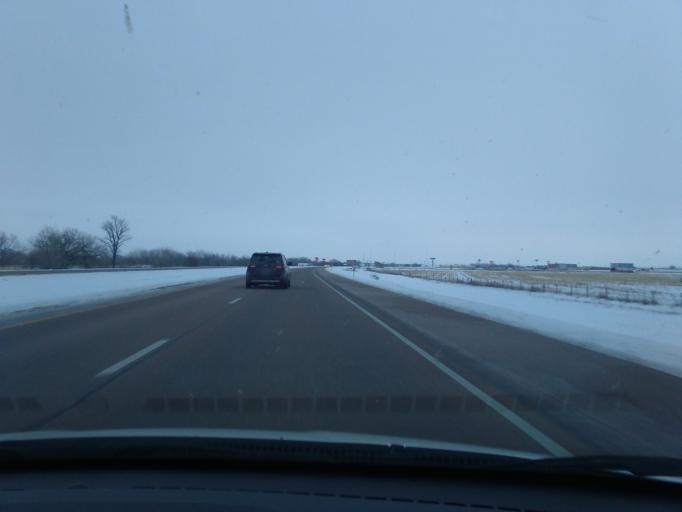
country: US
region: Nebraska
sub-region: Keith County
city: Ogallala
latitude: 41.1140
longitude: -101.7370
